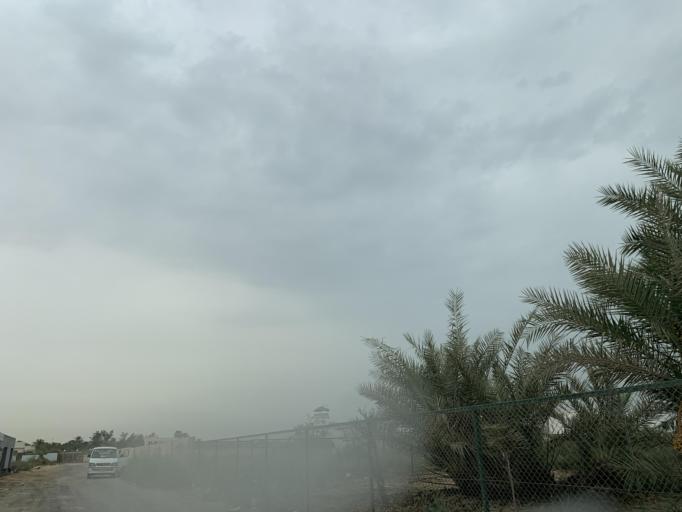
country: BH
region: Northern
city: Madinat `Isa
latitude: 26.1900
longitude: 50.4683
